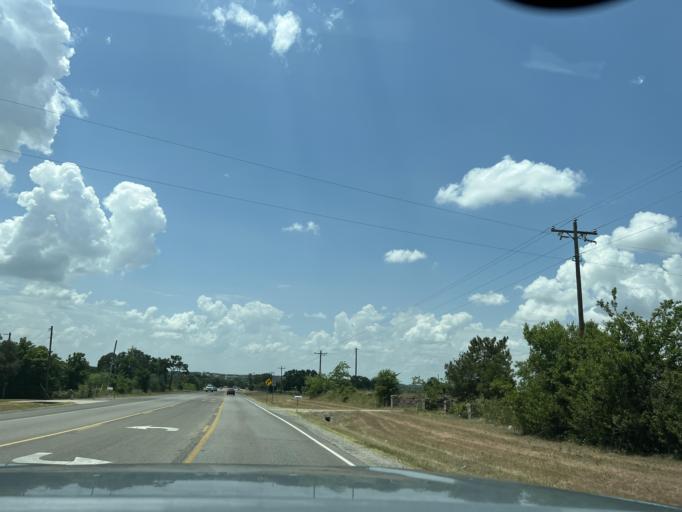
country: US
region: Texas
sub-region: Parker County
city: Weatherford
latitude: 32.8160
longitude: -97.7775
